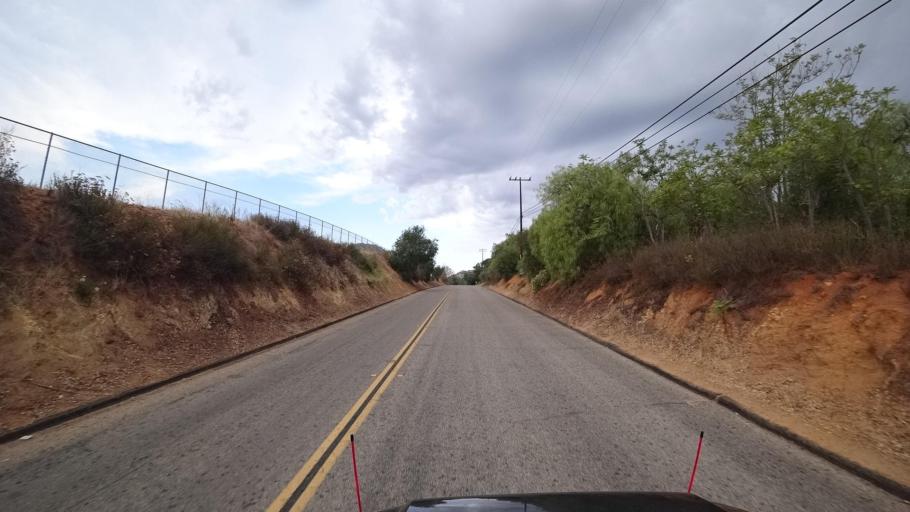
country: US
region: California
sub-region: San Diego County
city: Ramona
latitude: 32.9997
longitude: -116.9317
